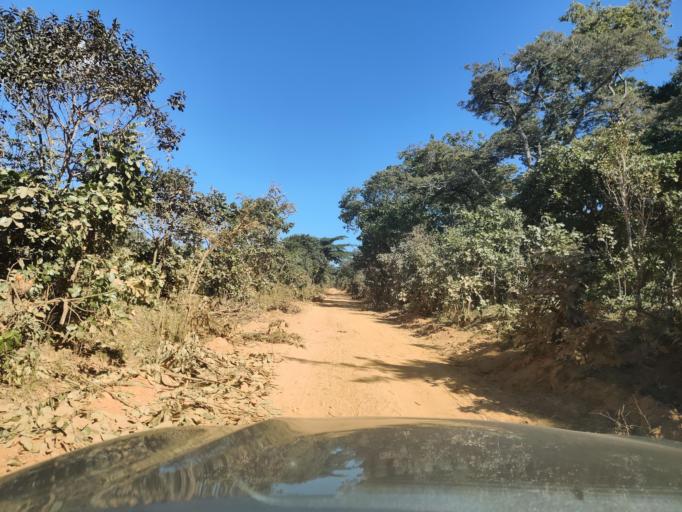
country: ZM
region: Central
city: Kapiri Mposhi
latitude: -13.5308
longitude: 28.8562
